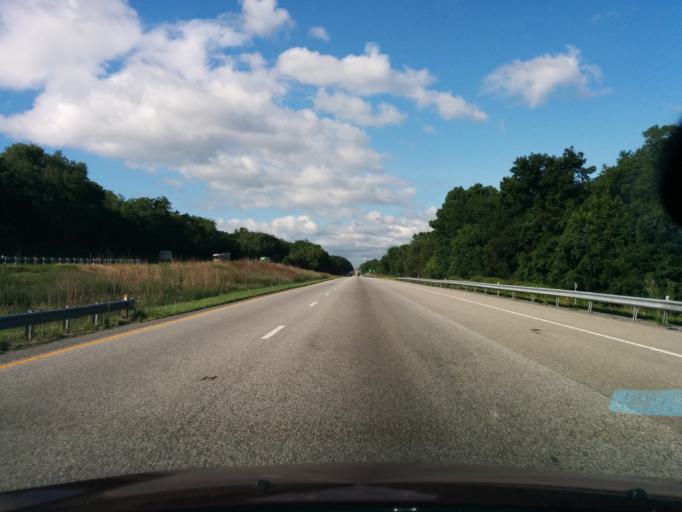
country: US
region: Virginia
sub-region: Rockbridge County
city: East Lexington
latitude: 37.7516
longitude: -79.4139
